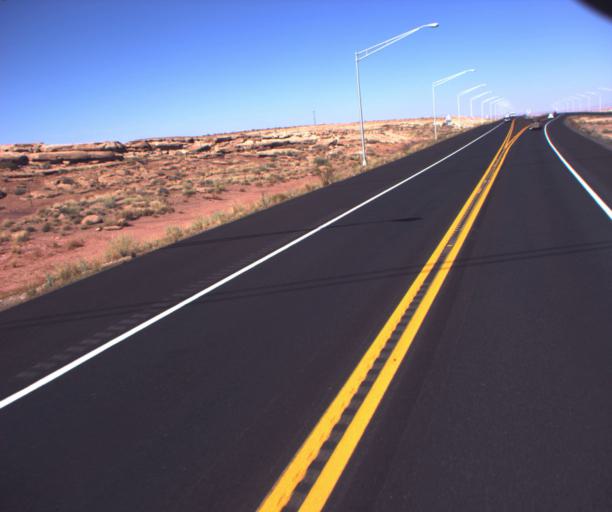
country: US
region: Arizona
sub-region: Coconino County
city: Tuba City
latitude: 35.8337
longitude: -111.4374
